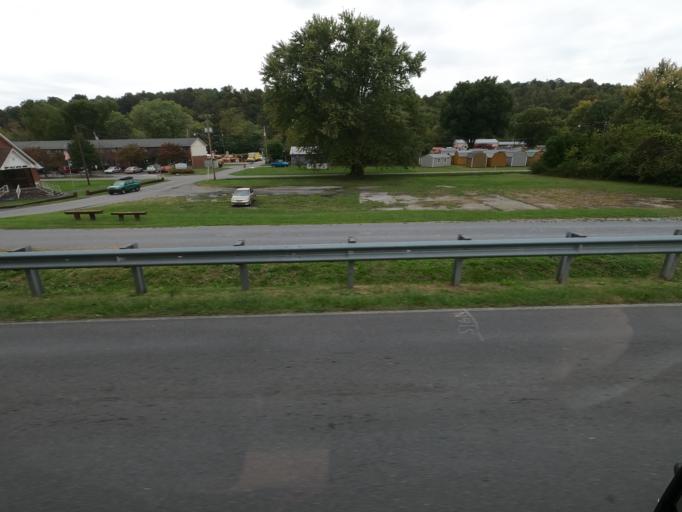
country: US
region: Tennessee
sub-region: Carter County
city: Central
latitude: 36.3339
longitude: -82.2622
